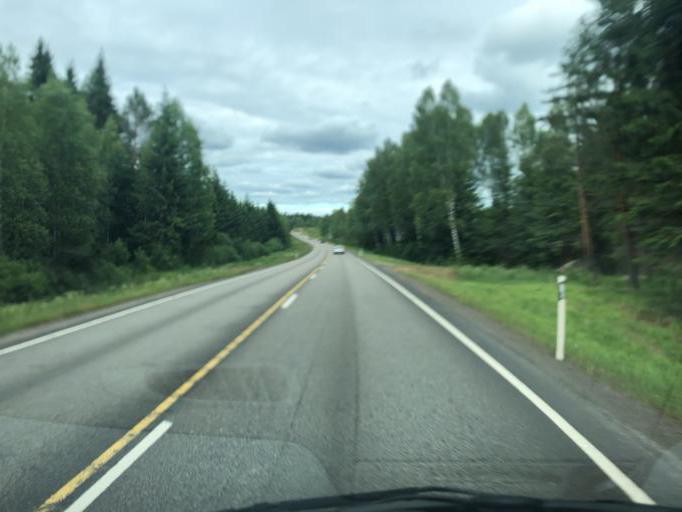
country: FI
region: Kymenlaakso
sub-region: Kouvola
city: Kouvola
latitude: 60.9991
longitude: 26.9321
